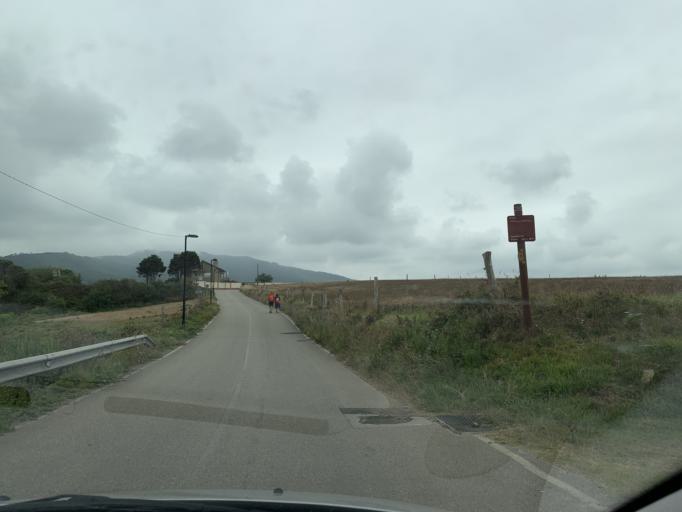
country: ES
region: Galicia
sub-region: Provincia de Lugo
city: Barreiros
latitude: 43.5536
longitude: -7.1470
